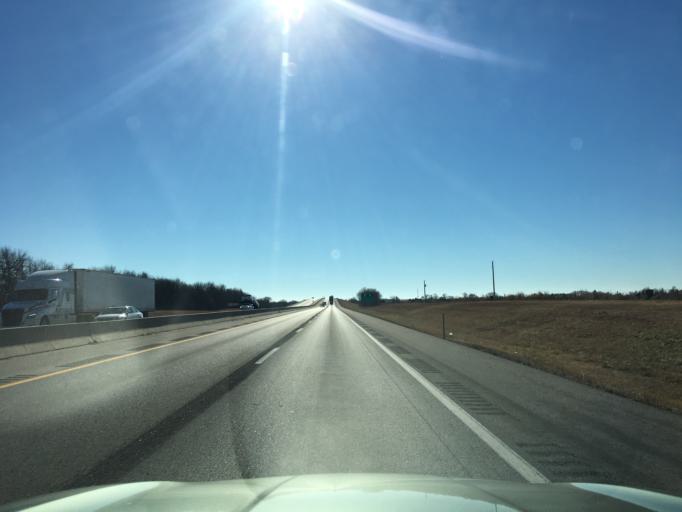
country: US
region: Kansas
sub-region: Sumner County
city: Wellington
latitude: 37.0796
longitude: -97.3386
